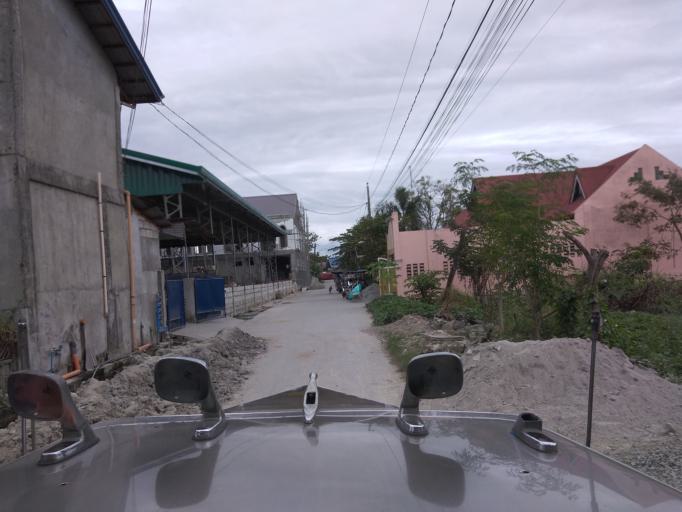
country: PH
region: Central Luzon
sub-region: Province of Pampanga
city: Mexico
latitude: 15.0619
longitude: 120.7254
